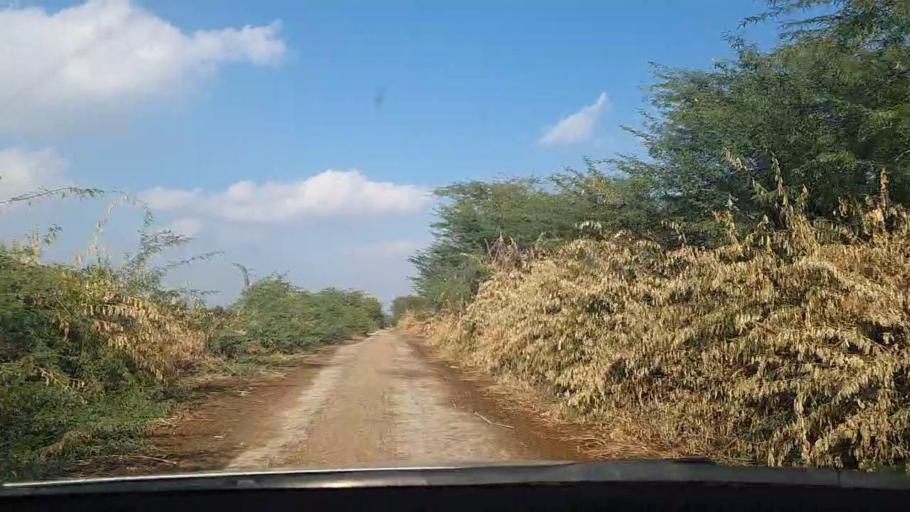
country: PK
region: Sindh
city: Tando Mittha Khan
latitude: 25.8813
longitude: 69.2945
